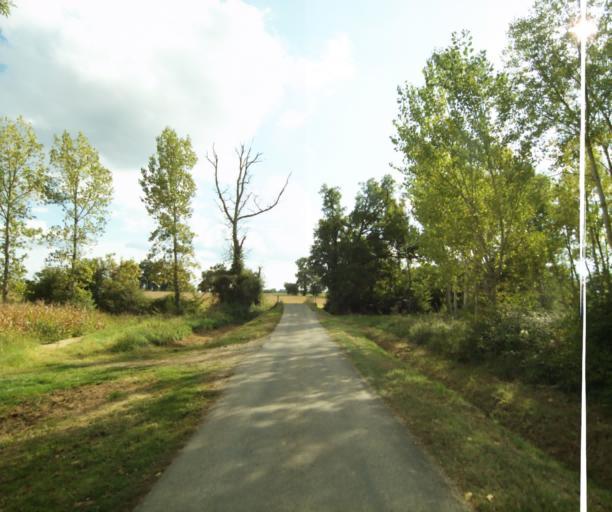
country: FR
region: Midi-Pyrenees
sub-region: Departement du Gers
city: Cazaubon
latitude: 43.9131
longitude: -0.0512
